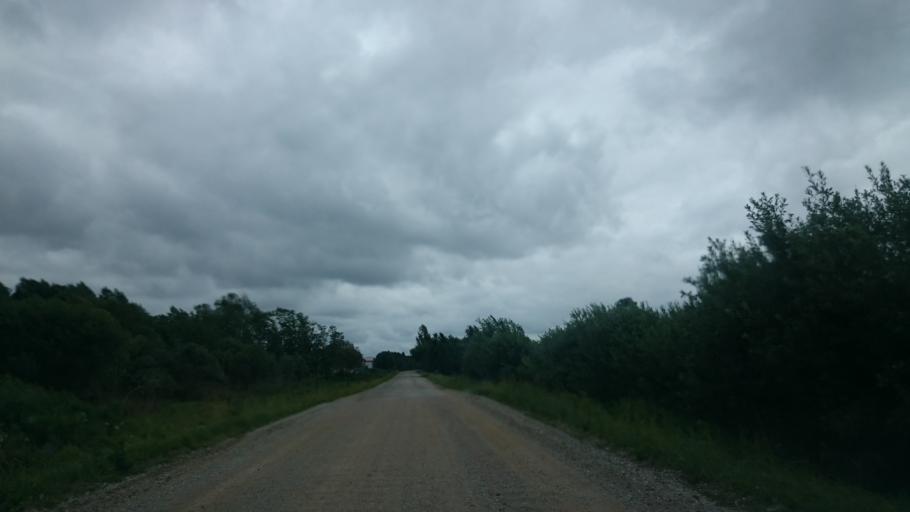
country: LV
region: Durbe
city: Liegi
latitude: 56.7484
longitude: 21.3659
